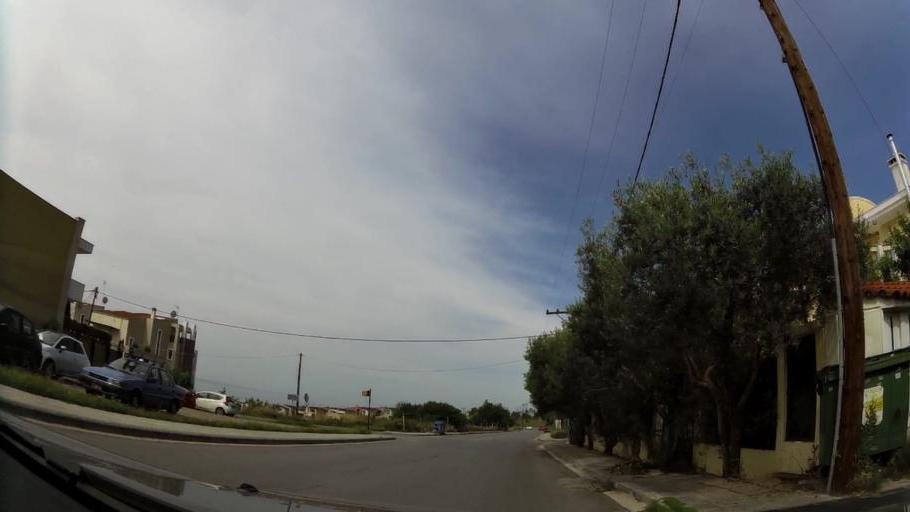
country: GR
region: Central Macedonia
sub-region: Nomos Thessalonikis
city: Panorama
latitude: 40.5777
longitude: 23.0188
